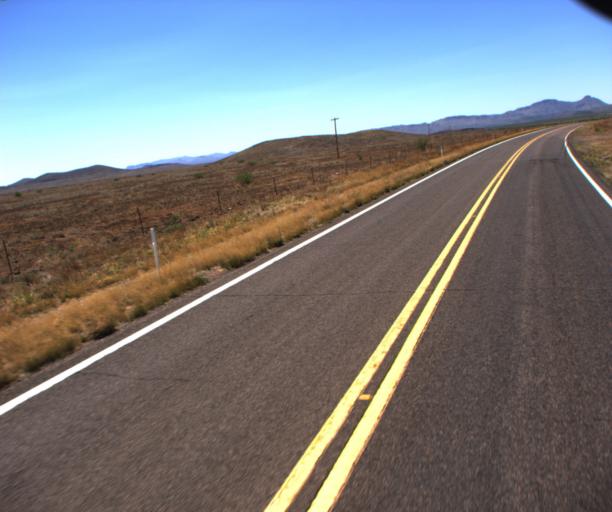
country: US
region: Arizona
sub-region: Cochise County
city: Douglas
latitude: 31.5522
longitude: -109.2703
